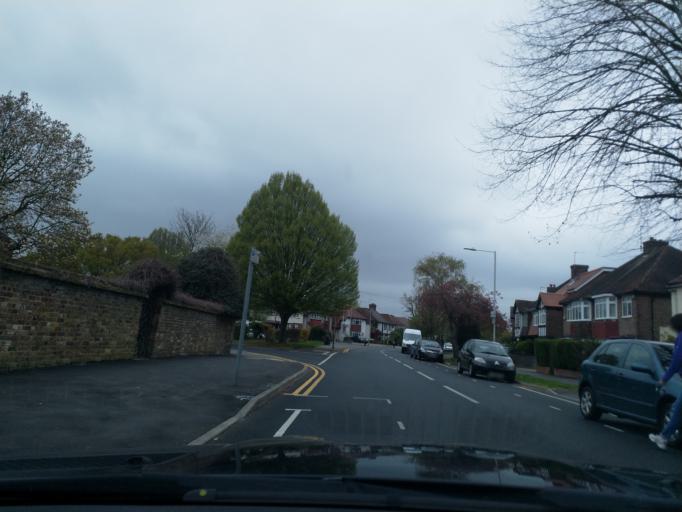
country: GB
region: England
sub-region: Greater London
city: Northolt
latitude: 51.5603
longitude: -0.3943
